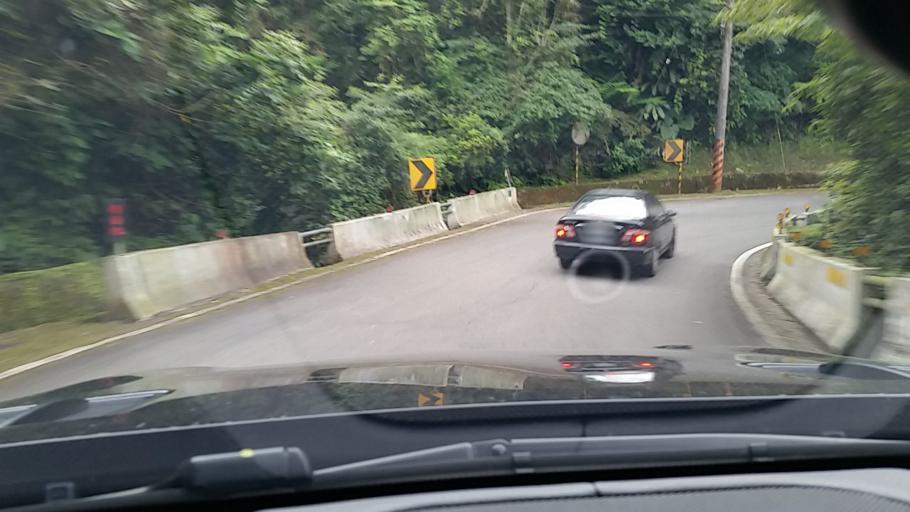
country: TW
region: Taiwan
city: Daxi
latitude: 24.8020
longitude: 121.2947
